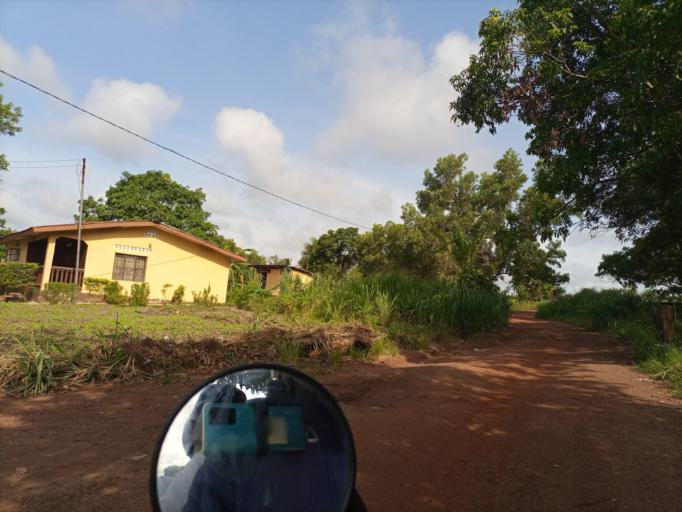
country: SL
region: Southern Province
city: Bo
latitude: 7.9650
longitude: -11.7622
